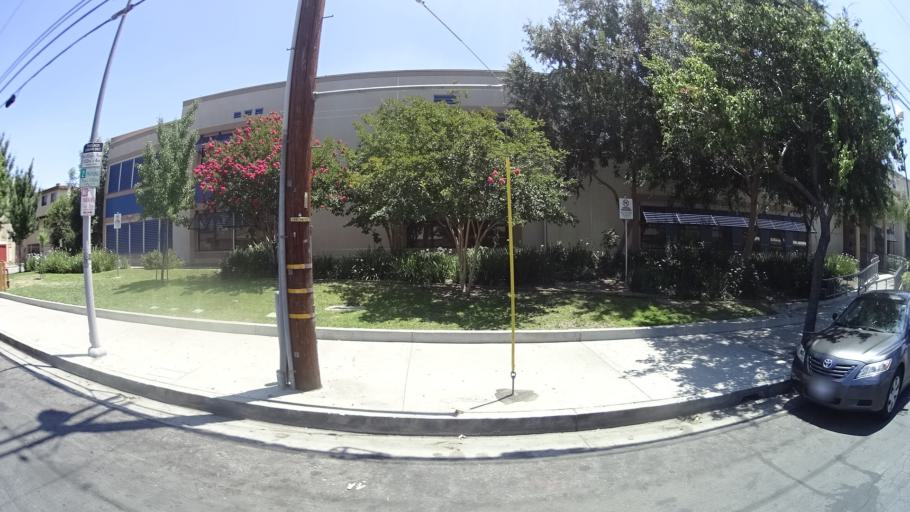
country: US
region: California
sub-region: Los Angeles County
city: Van Nuys
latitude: 34.2272
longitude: -118.4575
